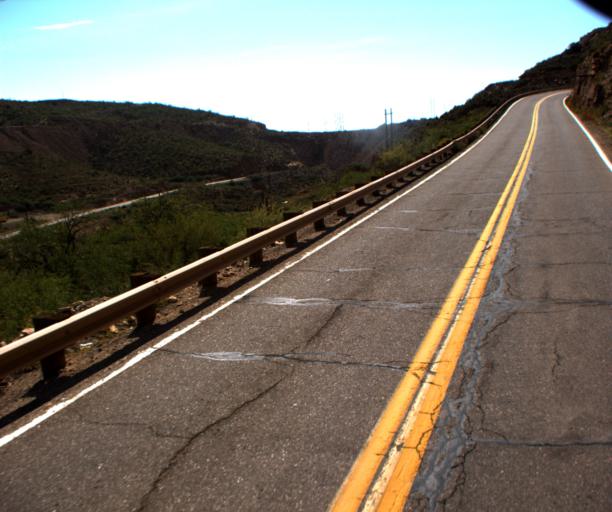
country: US
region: Arizona
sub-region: Greenlee County
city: Morenci
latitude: 33.0734
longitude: -109.3595
